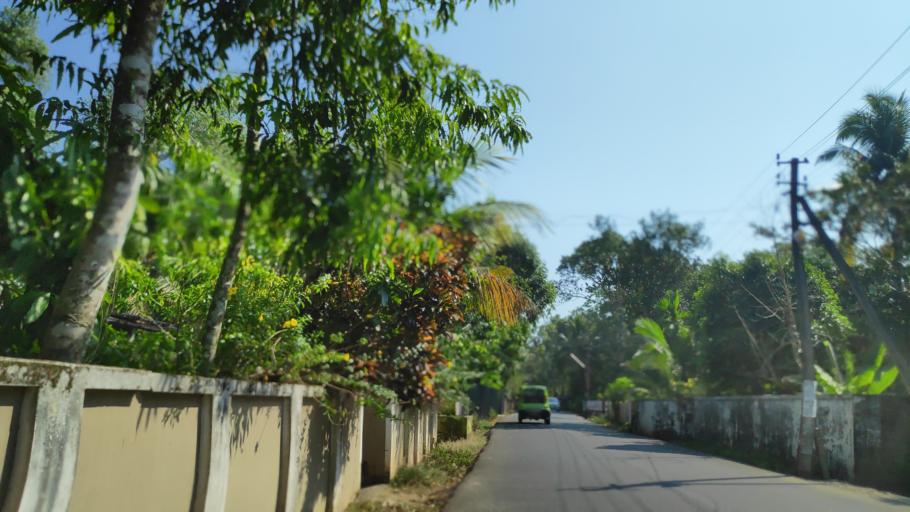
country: IN
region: Kerala
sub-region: Alappuzha
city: Alleppey
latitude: 9.5753
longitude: 76.3163
